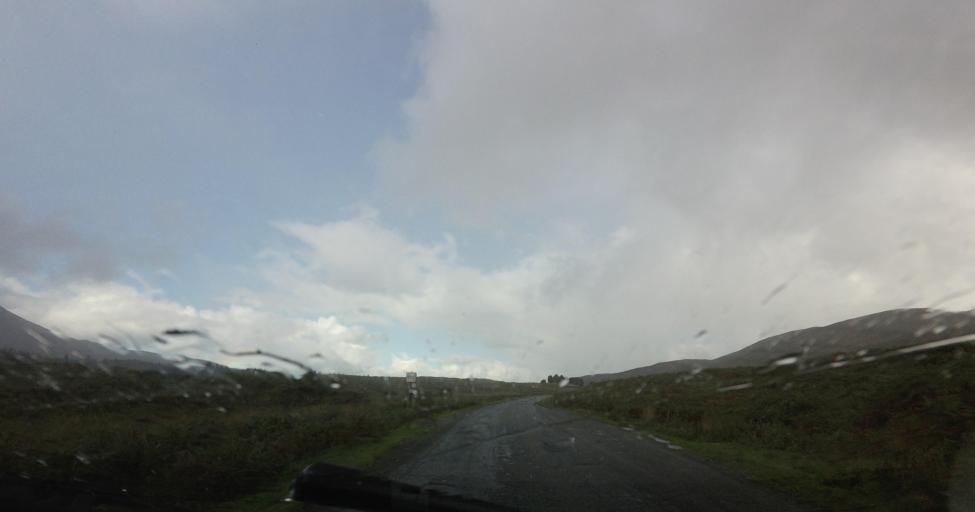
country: GB
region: Scotland
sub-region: Highland
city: Portree
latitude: 57.2131
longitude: -5.9515
